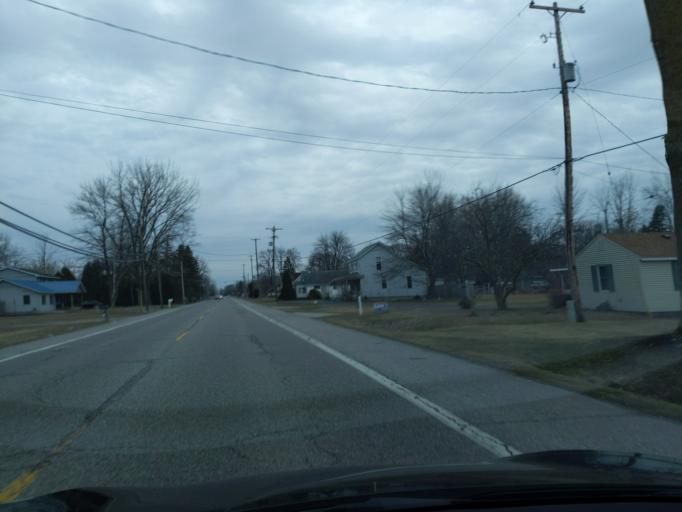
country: US
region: Michigan
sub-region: Bay County
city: Bay City
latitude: 43.6485
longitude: -83.9129
